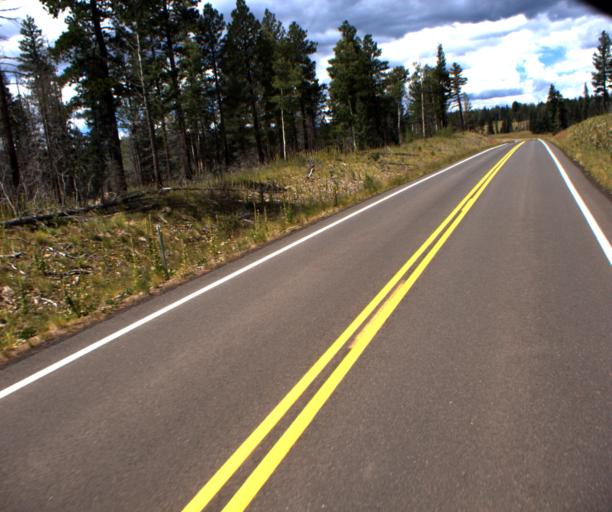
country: US
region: Arizona
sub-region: Apache County
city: Eagar
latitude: 33.9282
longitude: -109.4638
